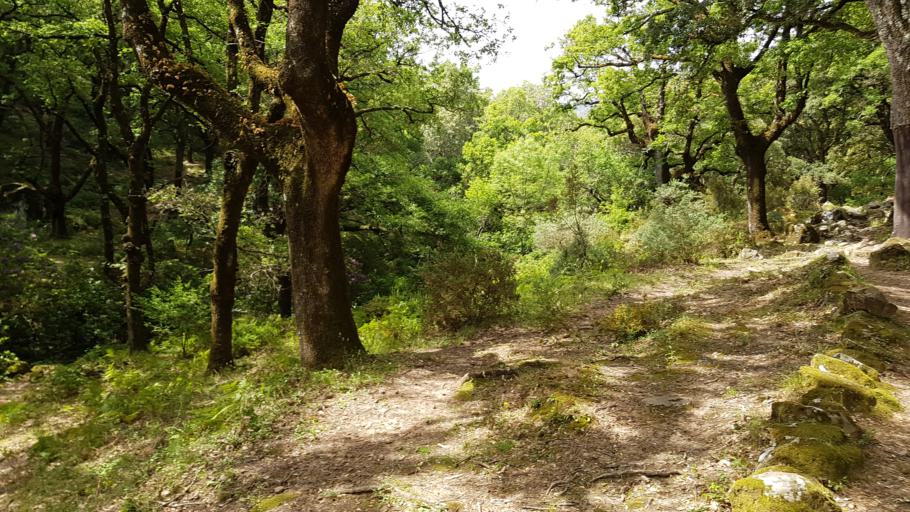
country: ES
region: Andalusia
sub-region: Provincia de Cadiz
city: Alcala de los Gazules
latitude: 36.5195
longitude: -5.5926
